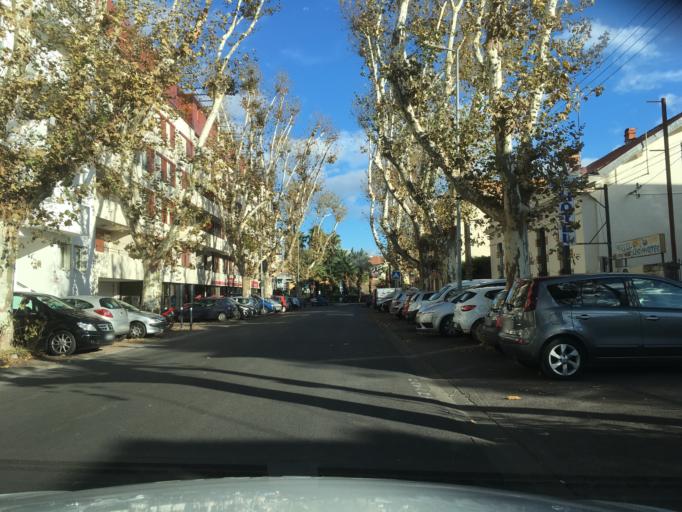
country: FR
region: Languedoc-Roussillon
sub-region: Departement de l'Herault
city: Montpellier
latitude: 43.6010
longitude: 3.8662
